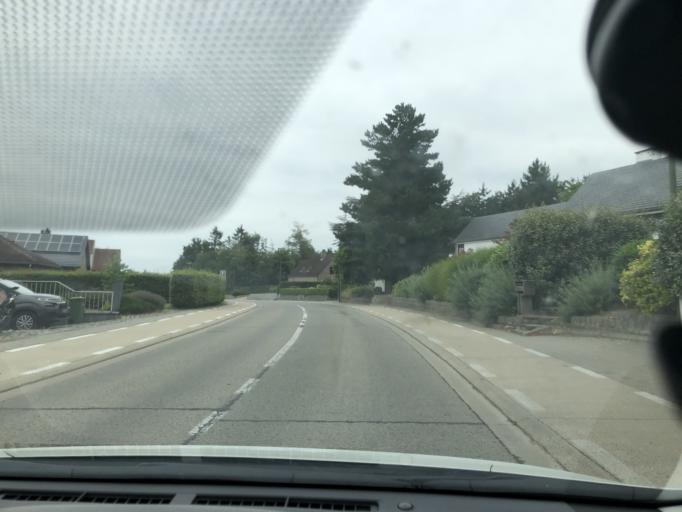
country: BE
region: Flanders
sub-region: Provincie Vlaams-Brabant
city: Oud-Heverlee
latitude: 50.8370
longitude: 4.6660
